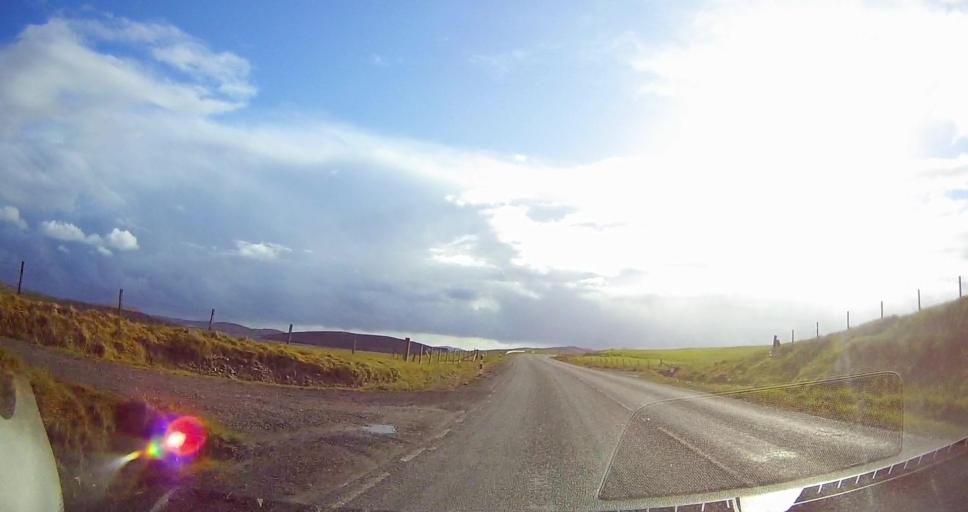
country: GB
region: Scotland
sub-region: Shetland Islands
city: Lerwick
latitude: 60.3714
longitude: -1.3198
